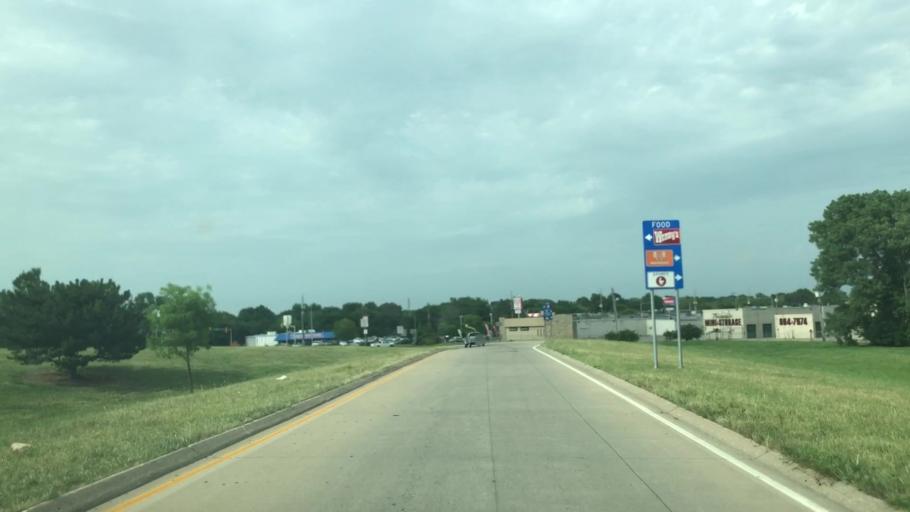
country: US
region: Oklahoma
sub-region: Tulsa County
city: Broken Arrow
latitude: 36.1173
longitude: -95.8590
